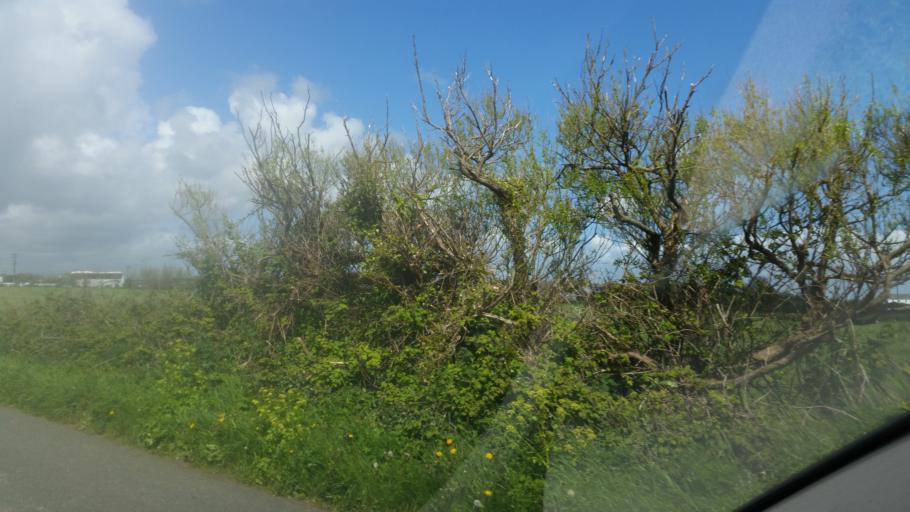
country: IE
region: Munster
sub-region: Waterford
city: Dunmore East
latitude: 52.1786
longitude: -6.8948
